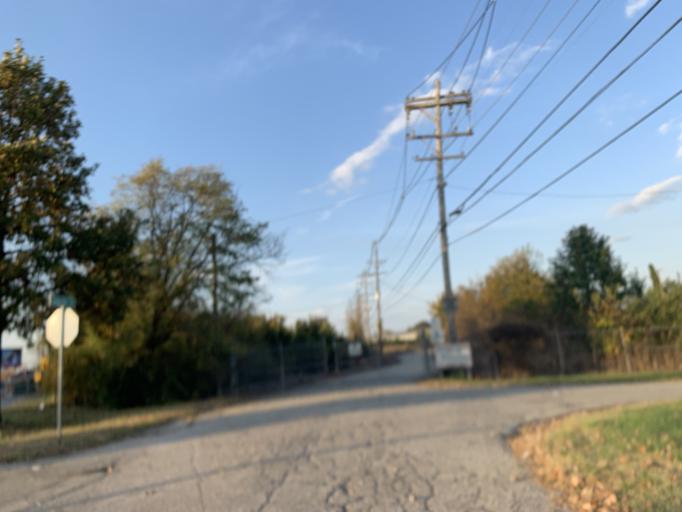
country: US
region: Kentucky
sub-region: Jefferson County
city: Shively
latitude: 38.2316
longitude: -85.8273
